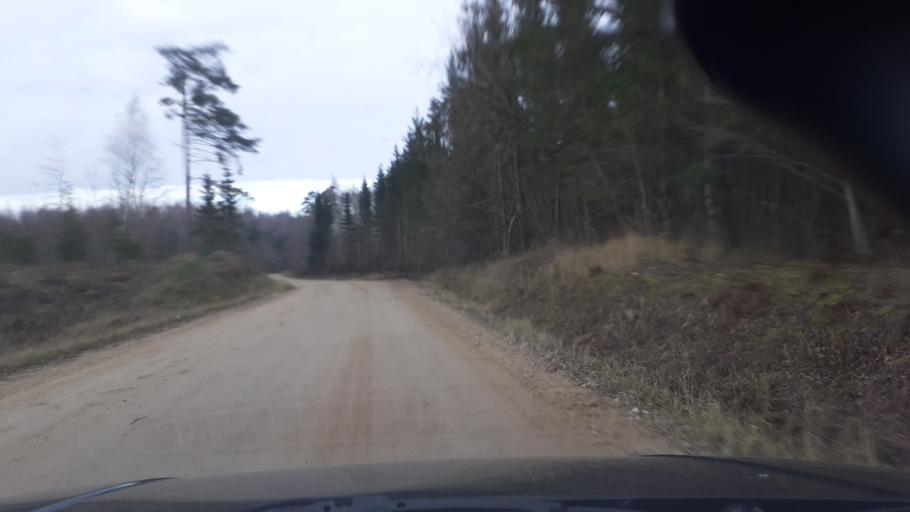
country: LV
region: Alsunga
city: Alsunga
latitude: 56.9930
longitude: 21.6732
